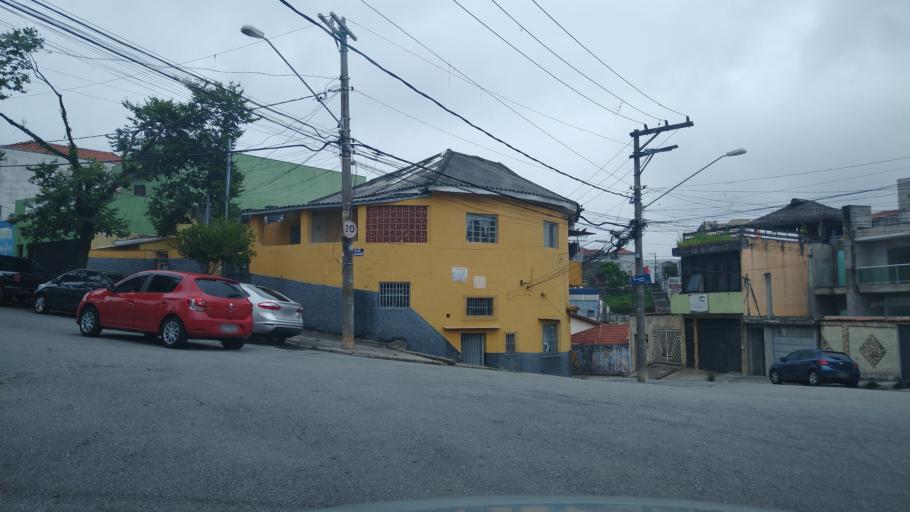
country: BR
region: Sao Paulo
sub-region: Sao Paulo
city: Sao Paulo
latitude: -23.5025
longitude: -46.5890
